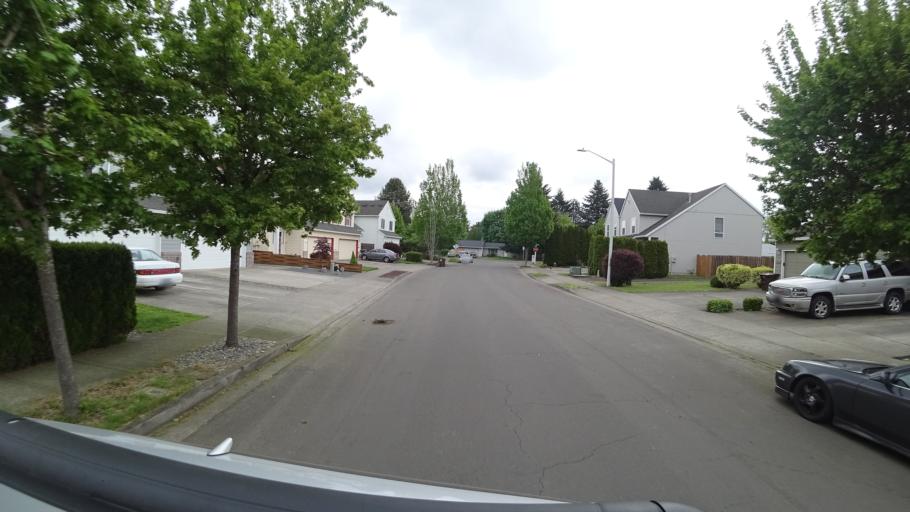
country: US
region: Oregon
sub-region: Washington County
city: Hillsboro
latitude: 45.5381
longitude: -122.9674
